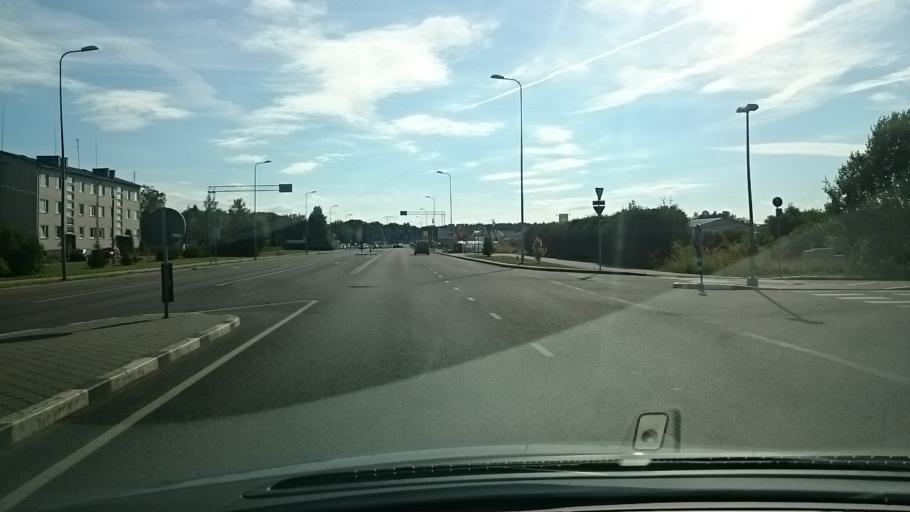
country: EE
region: Laeaene
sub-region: Ridala Parish
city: Uuemoisa
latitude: 58.9398
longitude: 23.5785
